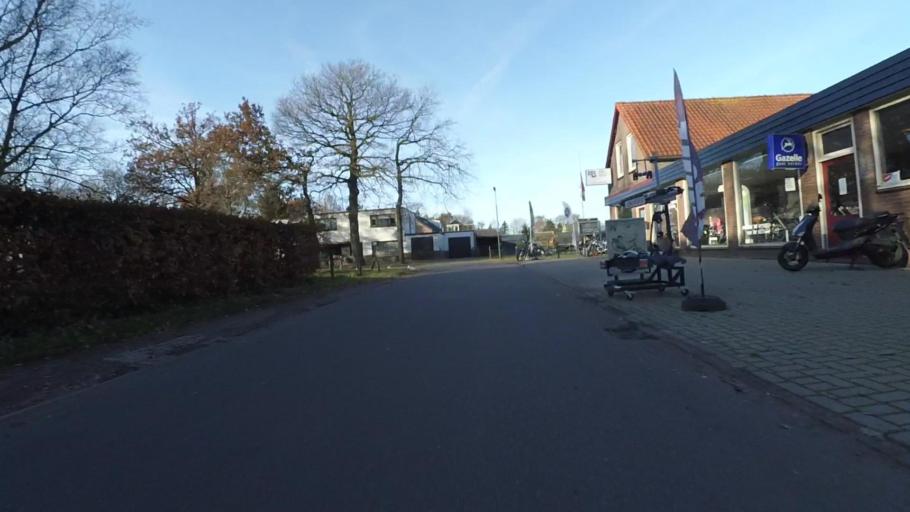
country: NL
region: Utrecht
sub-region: Gemeente Utrechtse Heuvelrug
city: Overberg
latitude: 52.0377
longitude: 5.5027
